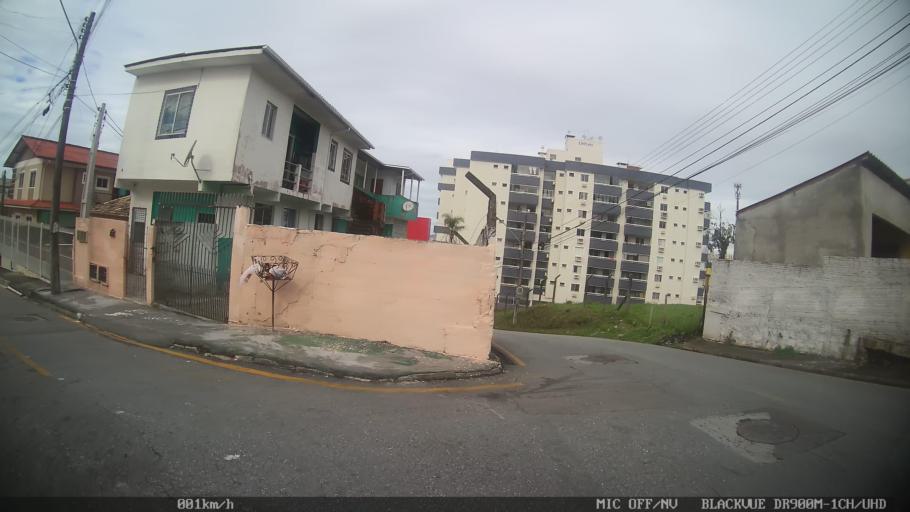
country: BR
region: Santa Catarina
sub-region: Sao Jose
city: Campinas
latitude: -27.5733
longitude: -48.6264
